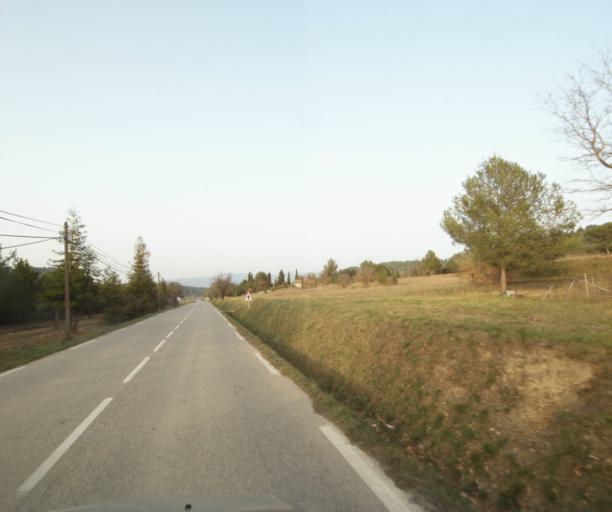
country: FR
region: Provence-Alpes-Cote d'Azur
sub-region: Departement des Bouches-du-Rhone
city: Rognes
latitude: 43.6909
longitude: 5.3427
